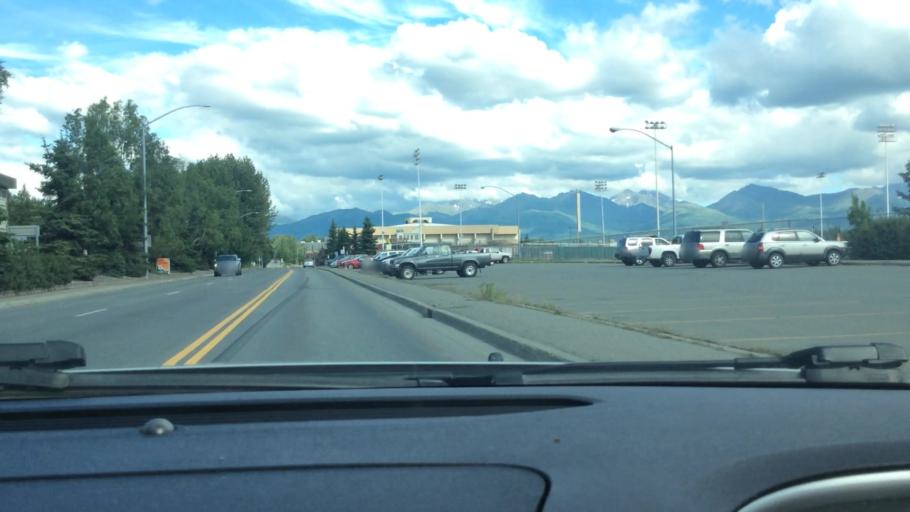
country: US
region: Alaska
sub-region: Anchorage Municipality
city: Anchorage
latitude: 61.2062
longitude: -149.8817
